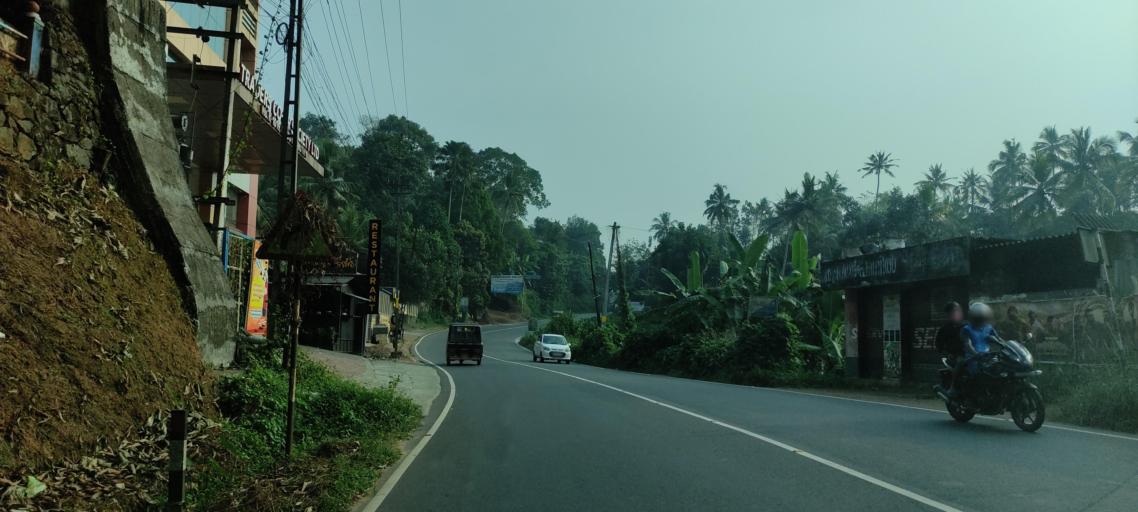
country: IN
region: Kerala
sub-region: Kottayam
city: Vaikam
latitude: 9.7626
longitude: 76.4930
